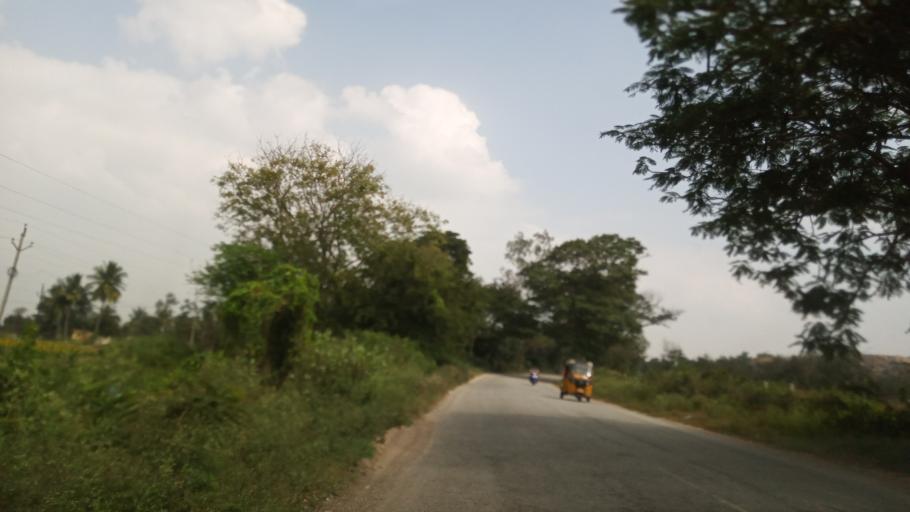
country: IN
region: Andhra Pradesh
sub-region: Chittoor
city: Madanapalle
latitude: 13.6454
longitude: 78.7249
